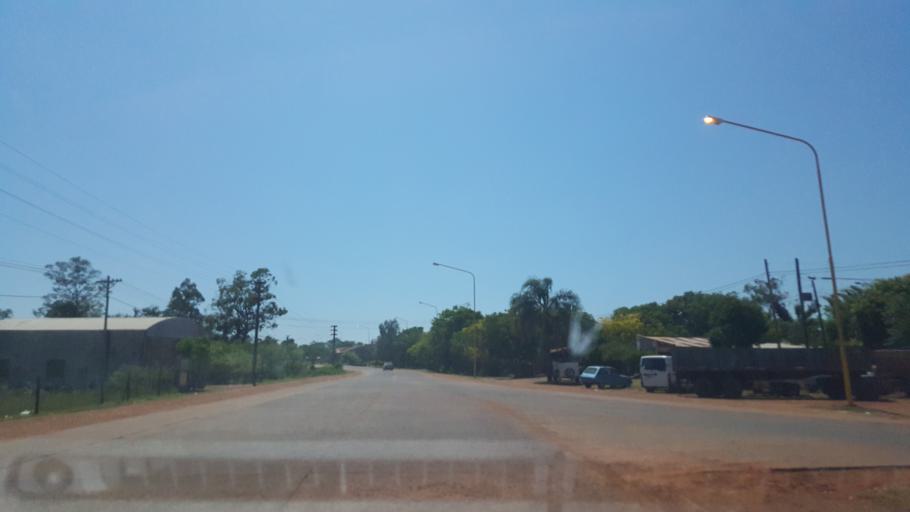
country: AR
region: Corrientes
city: Santo Tome
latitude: -28.5510
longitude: -56.0715
